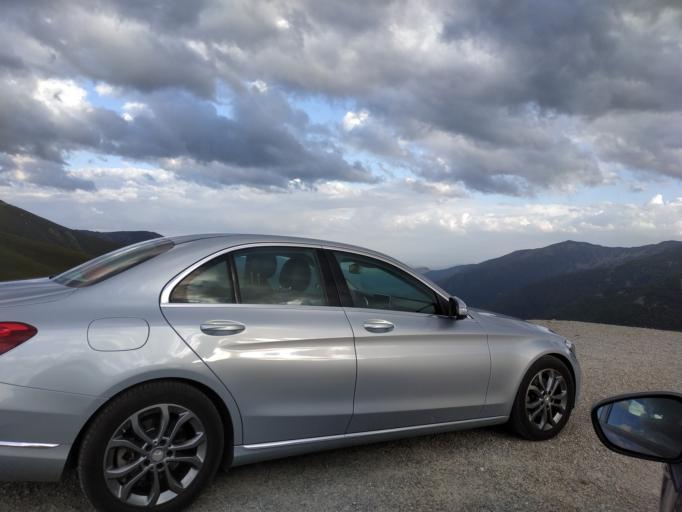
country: ES
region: Castille and Leon
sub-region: Provincia de Leon
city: Candin
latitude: 42.8685
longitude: -6.8181
